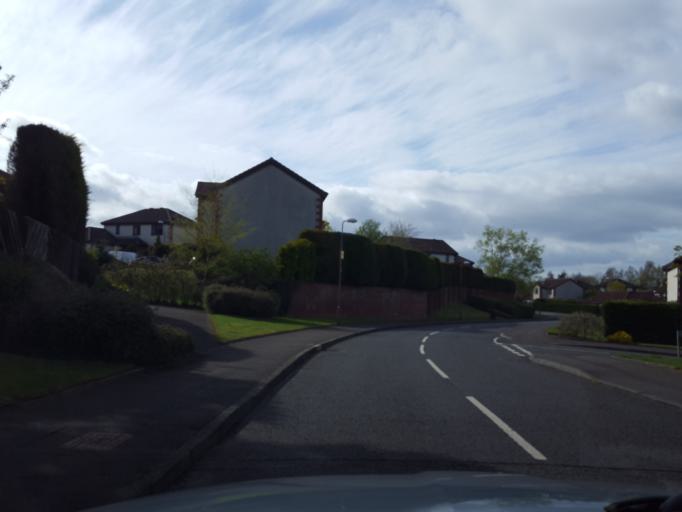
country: GB
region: Scotland
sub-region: West Lothian
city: Linlithgow
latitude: 55.9698
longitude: -3.6215
